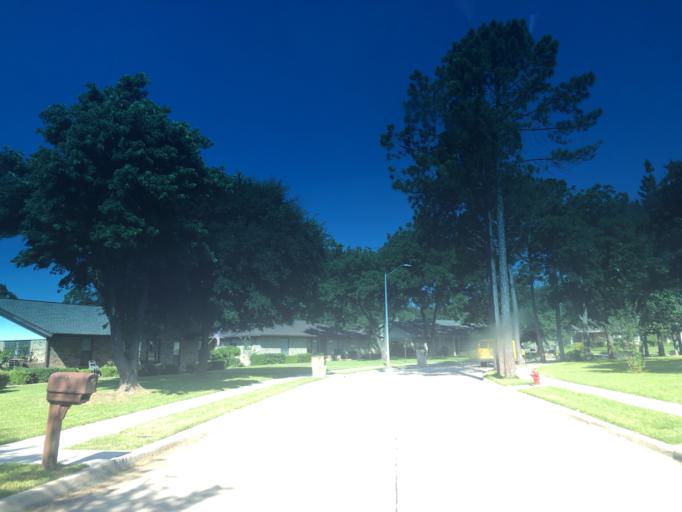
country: US
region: Texas
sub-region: Dallas County
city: Grand Prairie
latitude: 32.7155
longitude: -97.0171
